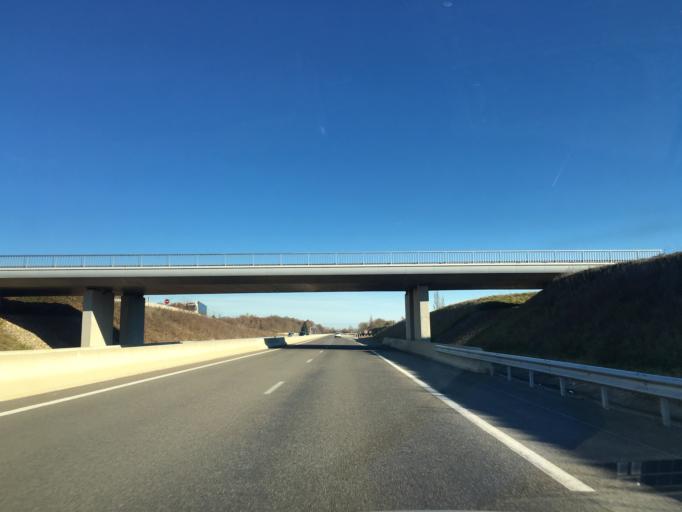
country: FR
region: Midi-Pyrenees
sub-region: Departement des Hautes-Pyrenees
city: Ossun
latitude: 43.1714
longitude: -0.0008
